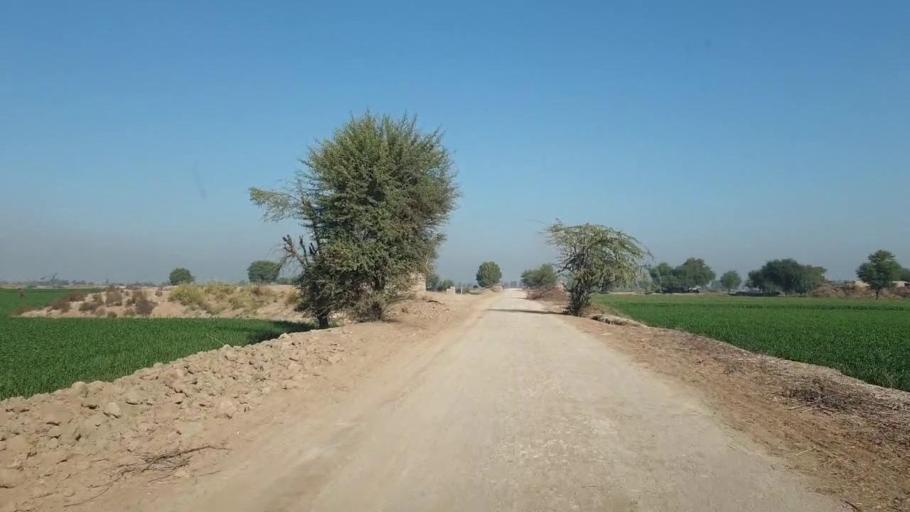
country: PK
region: Sindh
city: Shahdadpur
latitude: 25.9983
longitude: 68.4932
